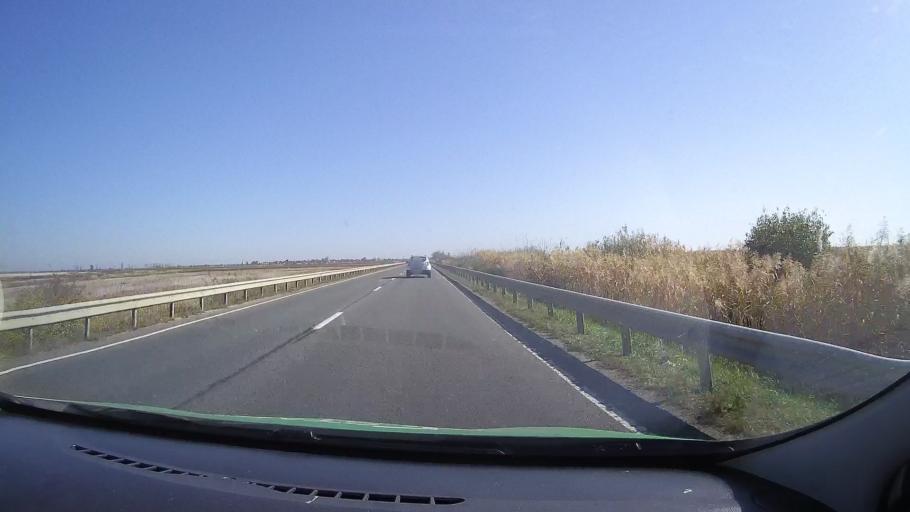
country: RO
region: Satu Mare
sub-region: Comuna Moftinu
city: Moftinu Mic
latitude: 47.6848
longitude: 22.5679
